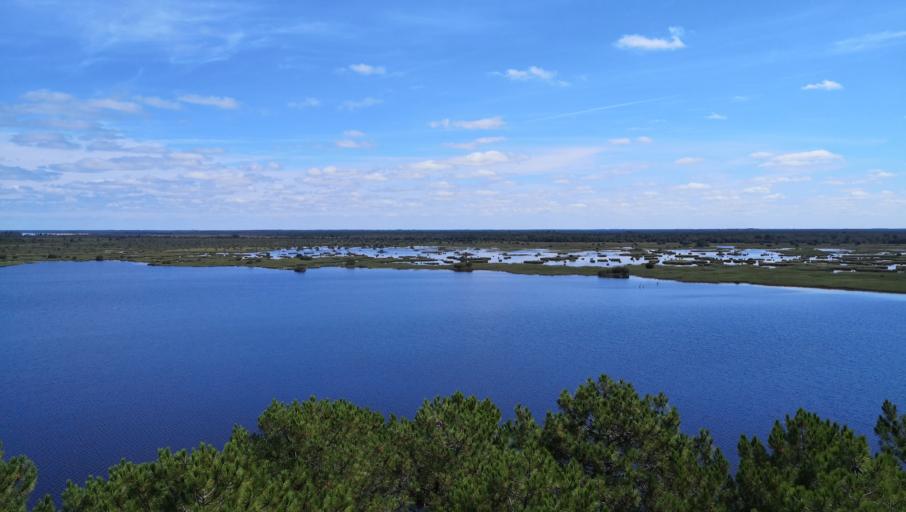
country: FR
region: Aquitaine
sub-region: Departement de la Gironde
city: Lacanau
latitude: 45.0356
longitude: -1.1459
